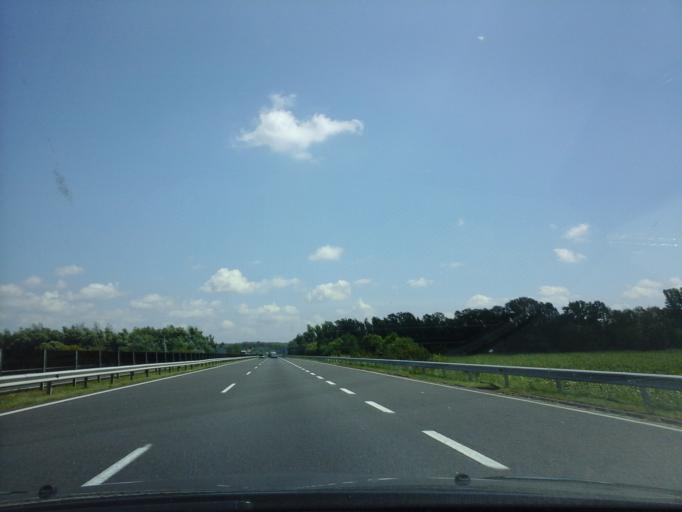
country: HU
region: Borsod-Abauj-Zemplen
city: Hejobaba
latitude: 47.8638
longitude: 21.0175
